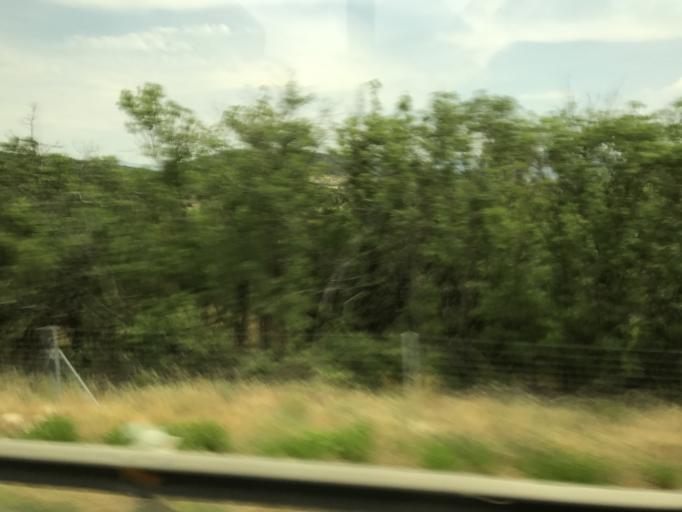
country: ES
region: Madrid
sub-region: Provincia de Madrid
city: Buitrago del Lozoya
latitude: 40.9462
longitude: -3.6377
